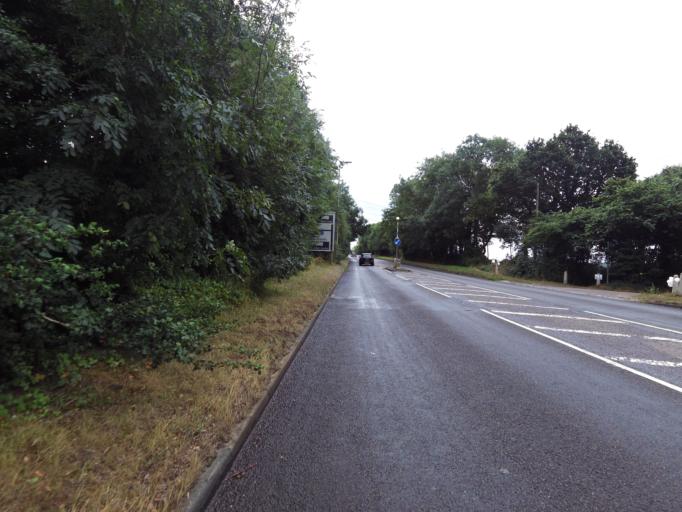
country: GB
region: England
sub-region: Hertfordshire
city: Radlett
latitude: 51.7005
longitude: -0.3264
